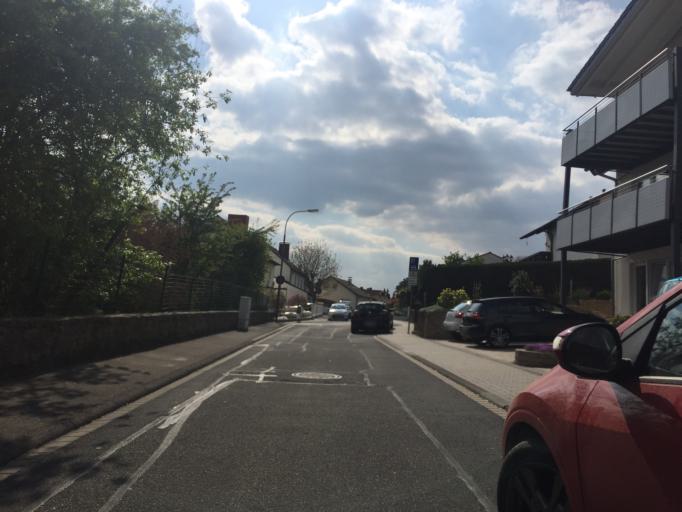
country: DE
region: Bavaria
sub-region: Regierungsbezirk Unterfranken
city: Goldbach
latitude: 49.9966
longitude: 9.1719
